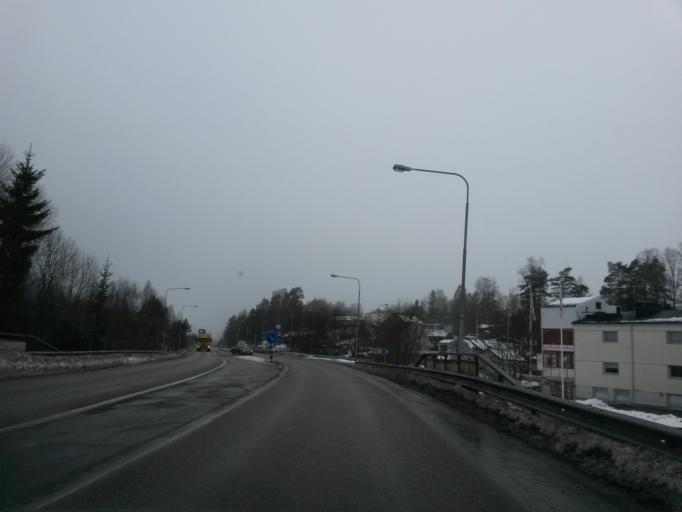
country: SE
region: Vaestra Goetaland
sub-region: Boras Kommun
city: Ganghester
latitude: 57.6975
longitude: 13.0263
